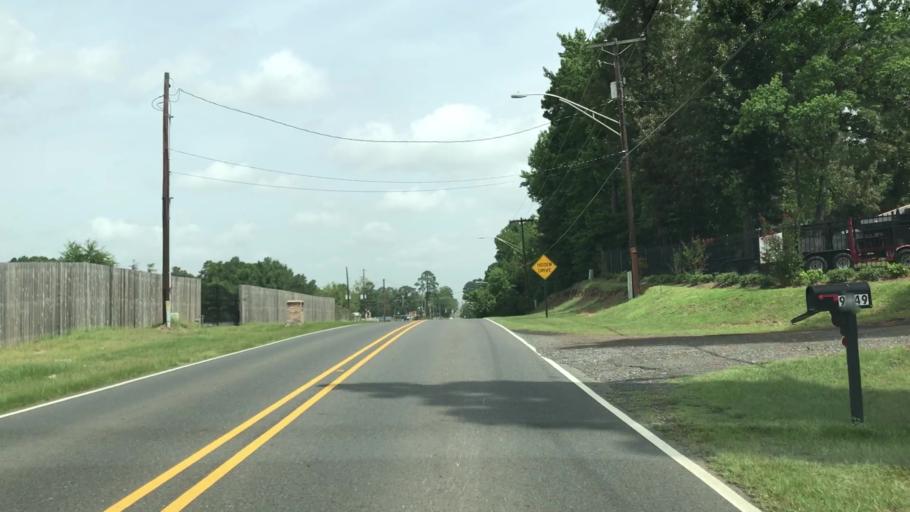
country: US
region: Louisiana
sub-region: De Soto Parish
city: Stonewall
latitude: 32.3878
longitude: -93.7634
